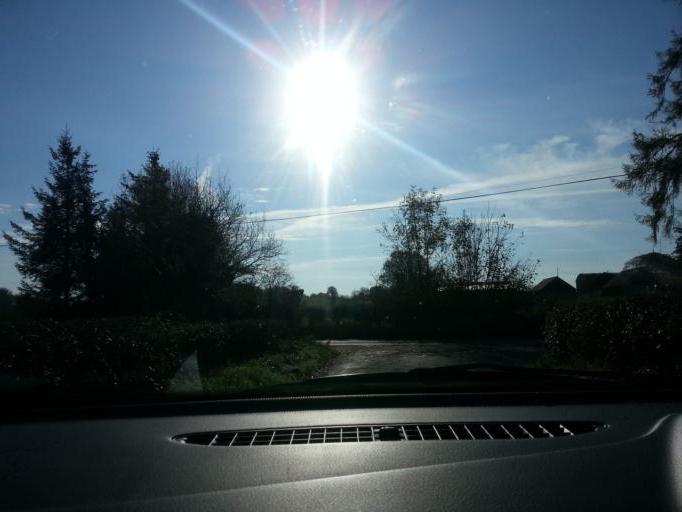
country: IE
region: Ulster
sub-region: County Monaghan
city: Clones
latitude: 54.2248
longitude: -7.3371
